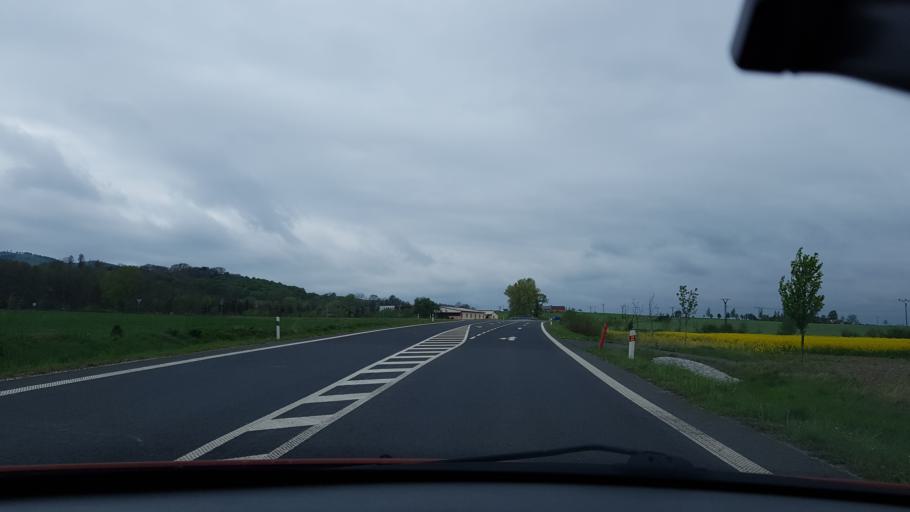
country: CZ
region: Olomoucky
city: Javornik
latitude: 50.4000
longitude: 17.0004
